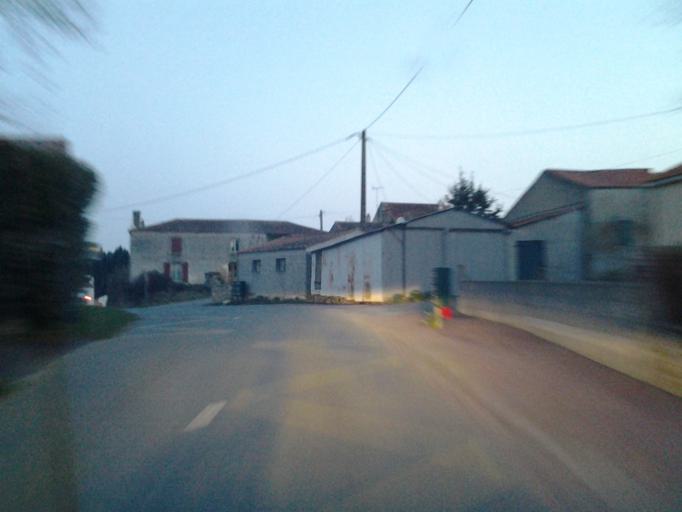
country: FR
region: Pays de la Loire
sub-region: Departement de la Vendee
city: Saint-Florent-des-Bois
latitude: 46.5831
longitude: -1.3560
